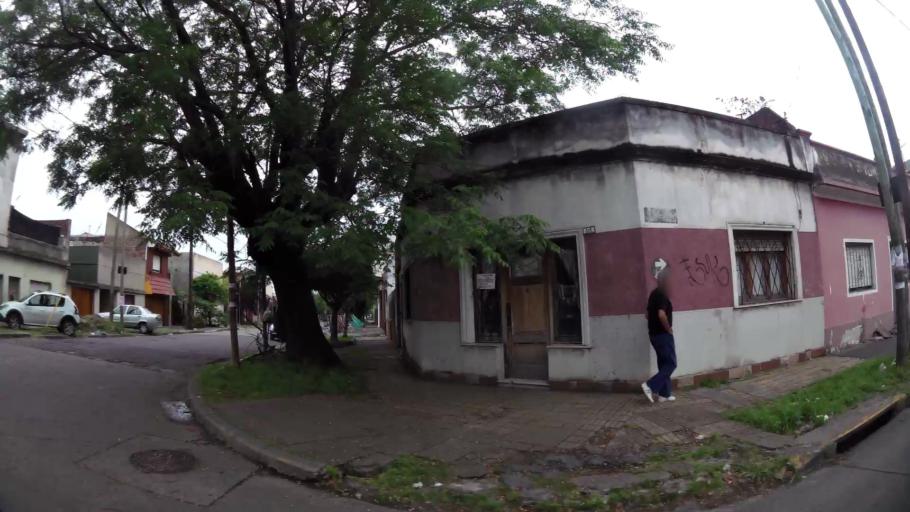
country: AR
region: Buenos Aires
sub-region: Partido de Lanus
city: Lanus
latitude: -34.7003
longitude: -58.3735
